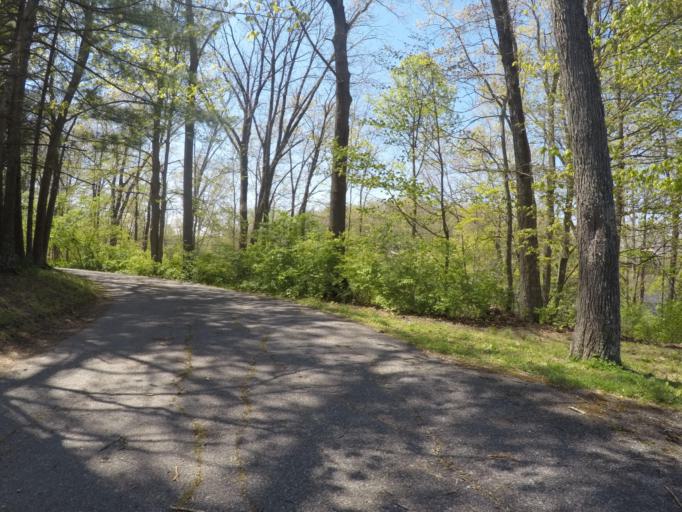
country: US
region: West Virginia
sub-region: Cabell County
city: Pea Ridge
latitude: 38.4066
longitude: -82.3246
